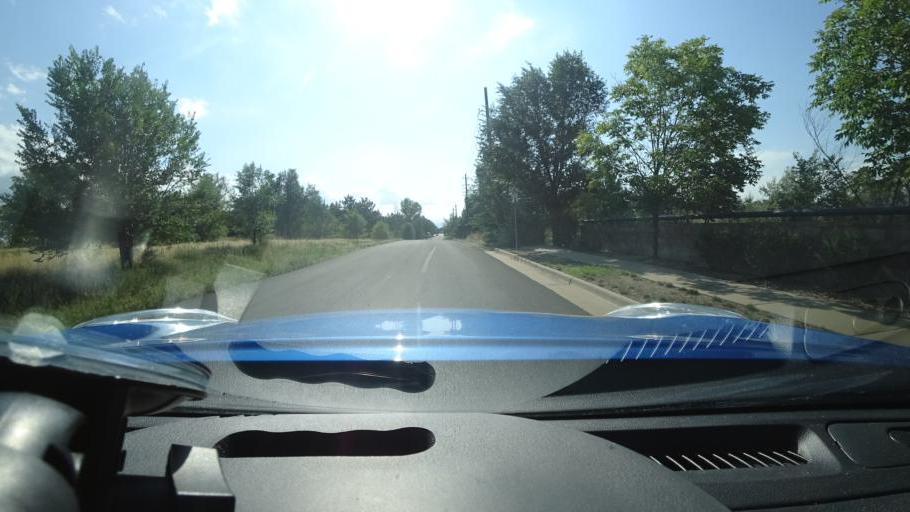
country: US
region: Colorado
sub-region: Adams County
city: Aurora
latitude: 39.6839
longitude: -104.8685
